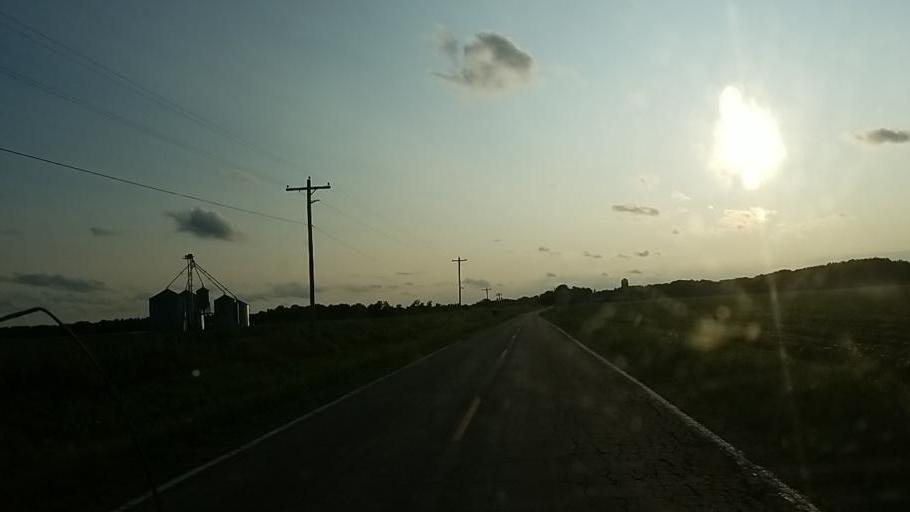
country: US
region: Michigan
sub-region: Montcalm County
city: Howard City
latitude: 43.3591
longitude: -85.3798
